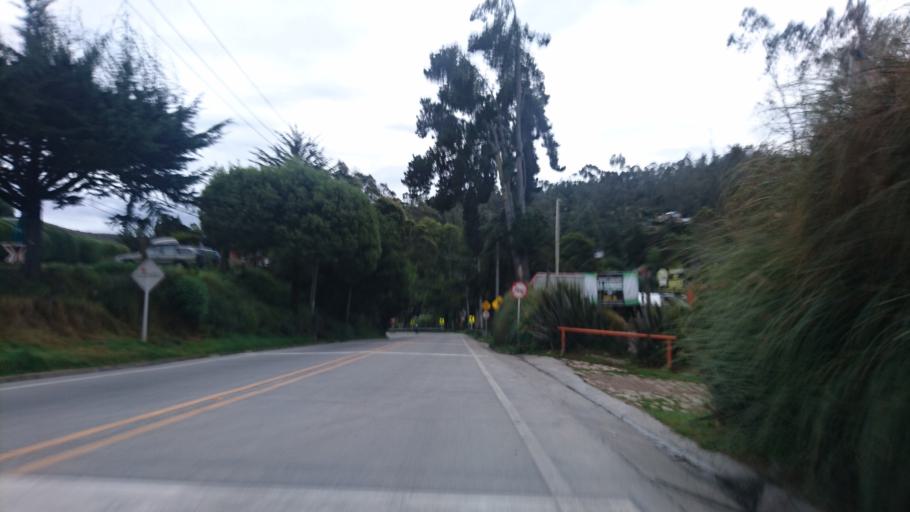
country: CO
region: Bogota D.C.
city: Barrio San Luis
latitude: 4.6671
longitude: -74.0135
